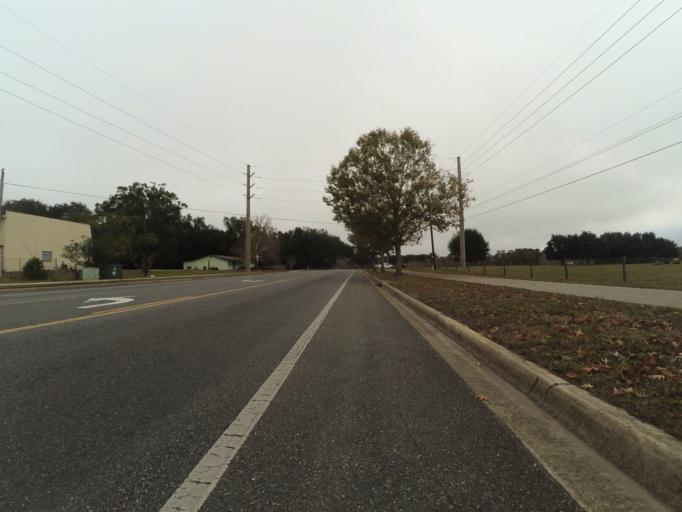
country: US
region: Florida
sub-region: Alachua County
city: Gainesville
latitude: 29.6213
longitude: -82.3558
